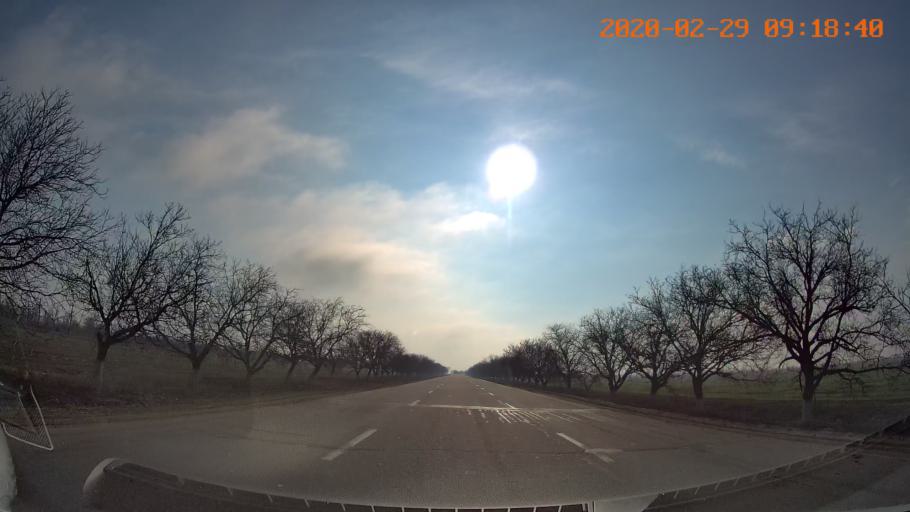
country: MD
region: Telenesti
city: Pervomaisc
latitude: 46.7714
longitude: 29.9272
